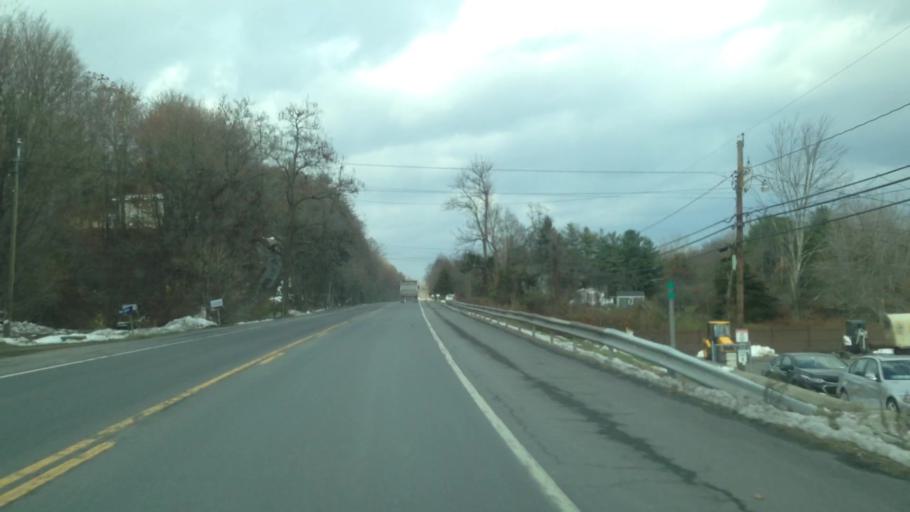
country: US
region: New York
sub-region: Ulster County
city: Lake Katrine
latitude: 41.9671
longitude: -73.9718
